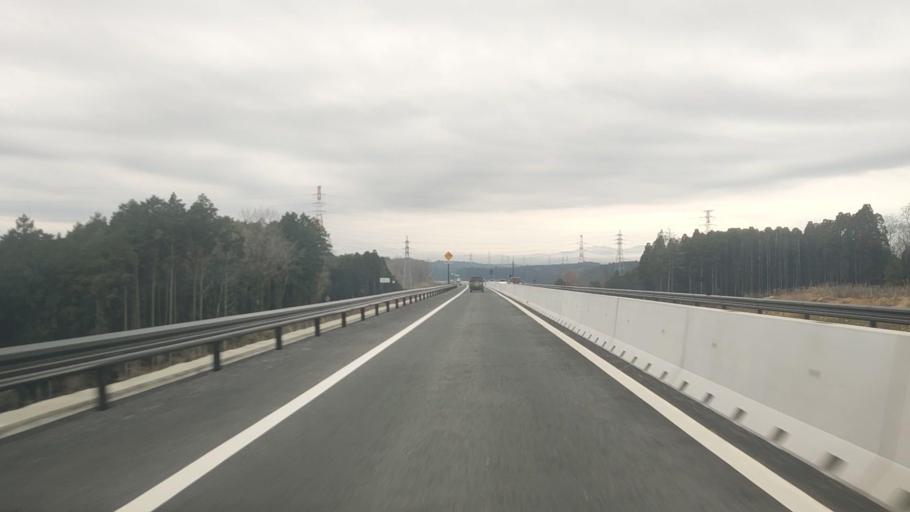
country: JP
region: Kumamoto
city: Ozu
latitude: 32.8999
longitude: 130.9180
